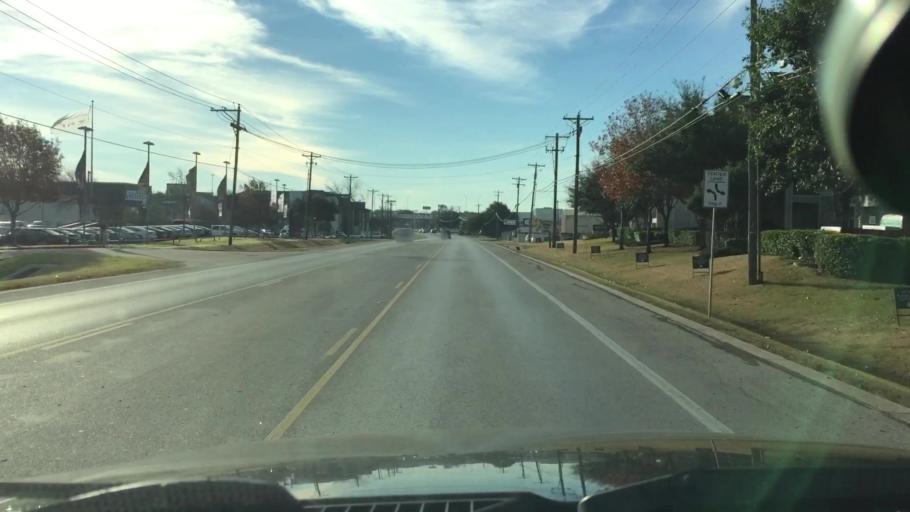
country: US
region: Texas
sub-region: Williamson County
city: Jollyville
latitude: 30.4403
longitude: -97.7730
